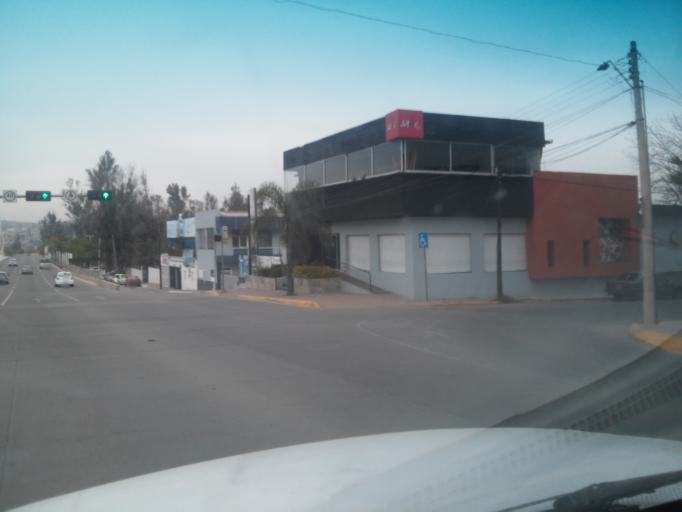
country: MX
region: Durango
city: Victoria de Durango
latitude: 24.0219
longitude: -104.6900
